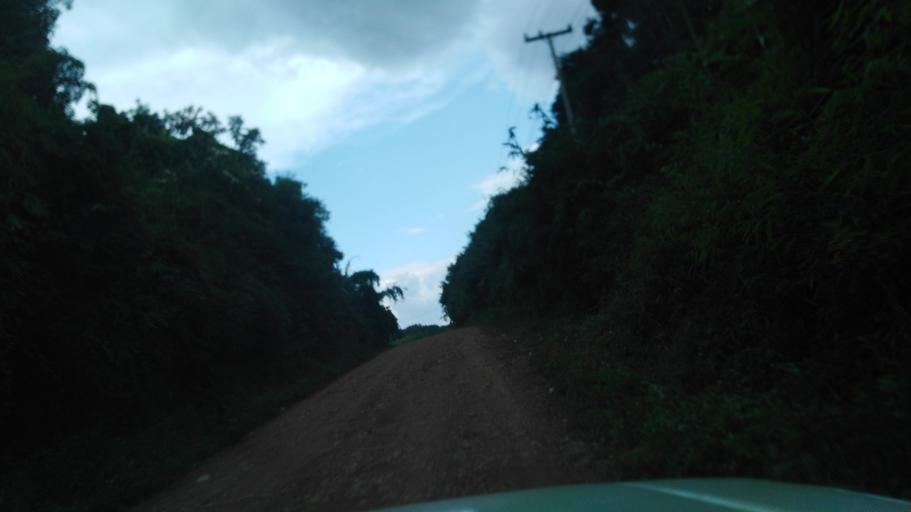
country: TH
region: Nan
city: Chaloem Phra Kiat
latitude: 19.7191
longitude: 100.7672
